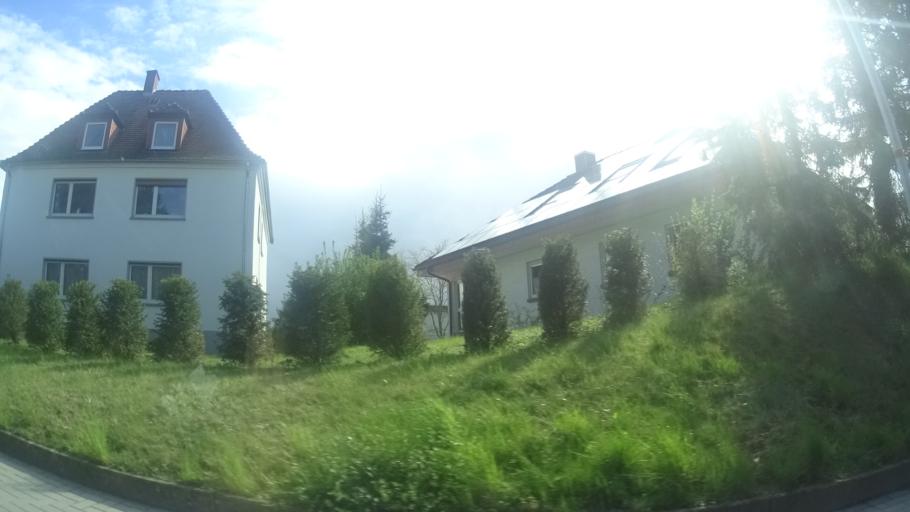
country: DE
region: Hesse
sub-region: Regierungsbezirk Giessen
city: Hoernsheim
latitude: 50.5114
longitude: 8.6236
